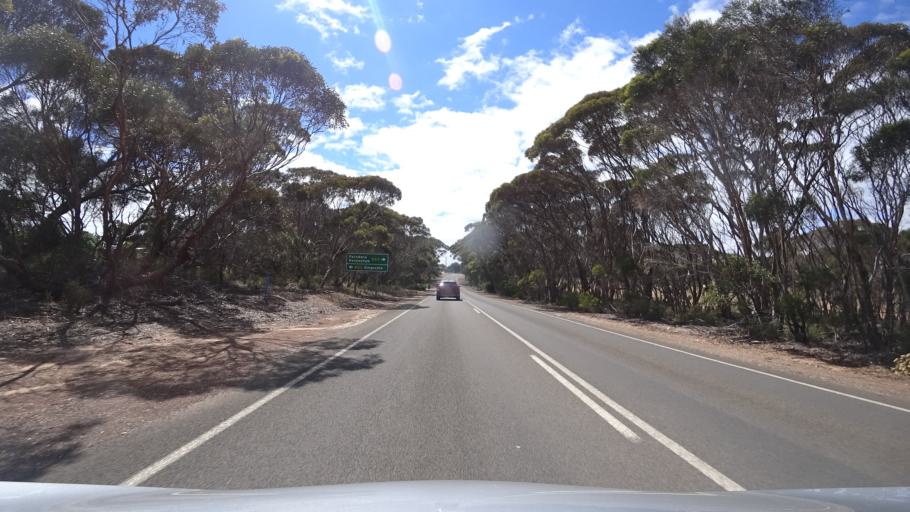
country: AU
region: South Australia
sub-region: Kangaroo Island
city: Kingscote
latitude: -35.6613
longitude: 137.5980
